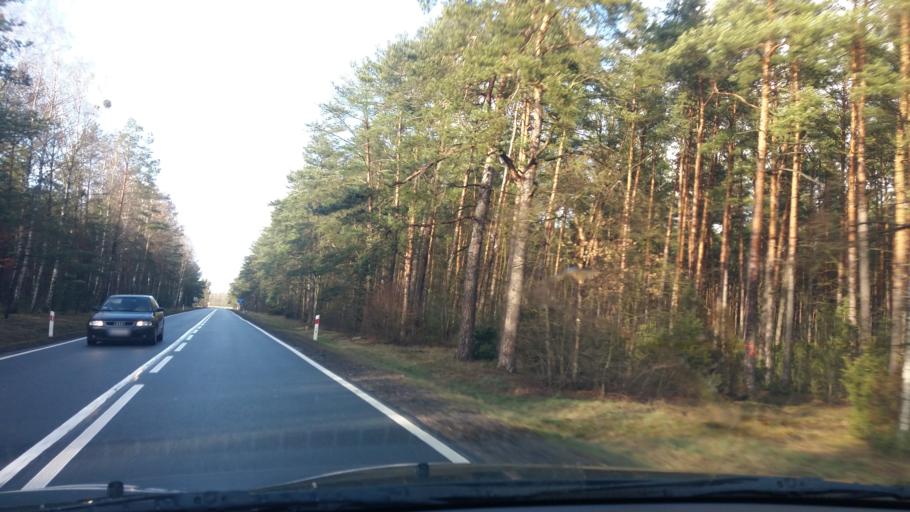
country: PL
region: Masovian Voivodeship
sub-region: Powiat przasnyski
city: Chorzele
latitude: 53.3158
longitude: 20.9092
